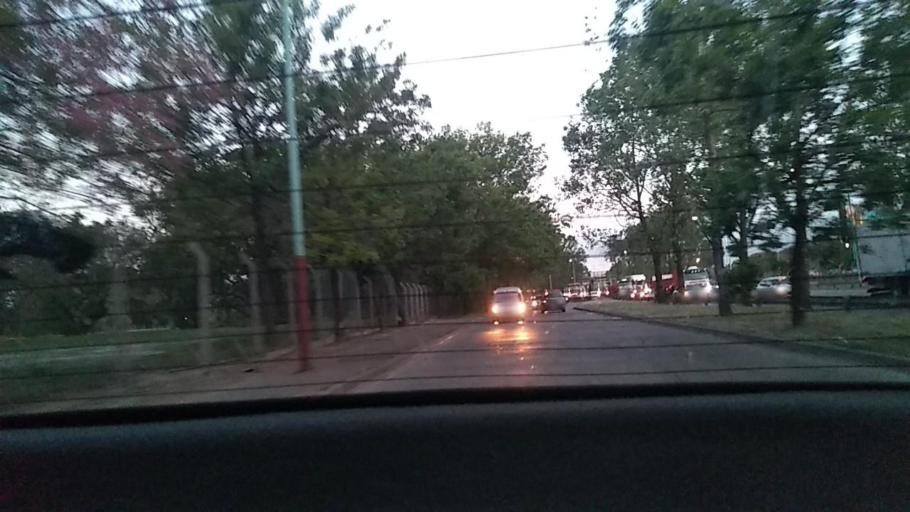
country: AR
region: Buenos Aires F.D.
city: Colegiales
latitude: -34.5461
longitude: -58.4416
